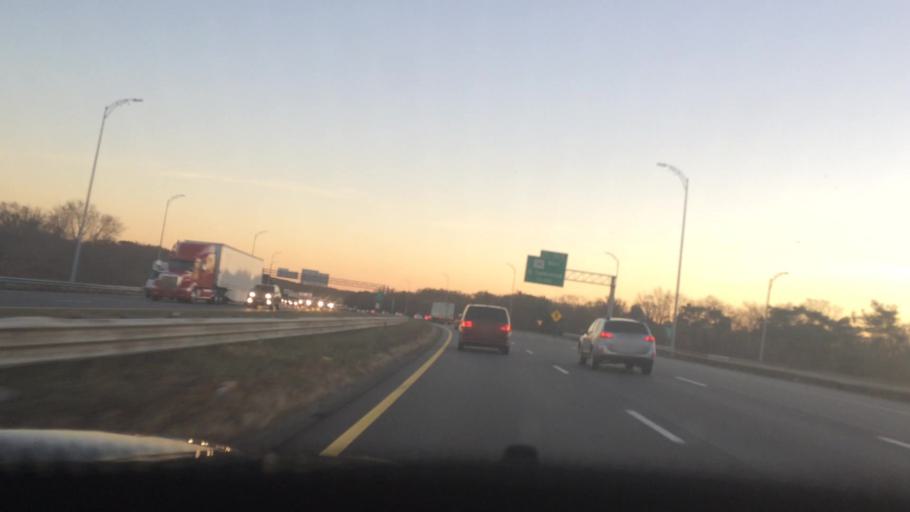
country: US
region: Massachusetts
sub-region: Essex County
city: North Andover
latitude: 42.6968
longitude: -71.1425
